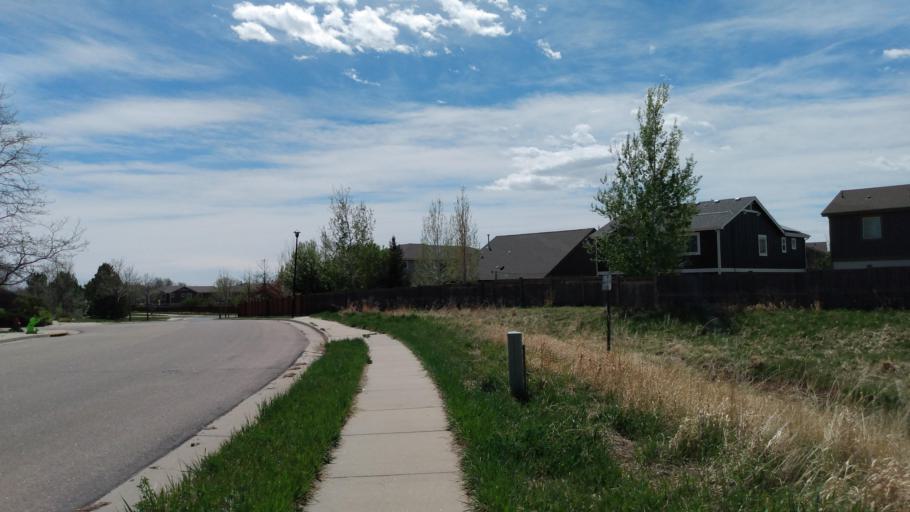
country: US
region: Colorado
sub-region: Boulder County
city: Lafayette
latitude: 40.0078
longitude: -105.0963
